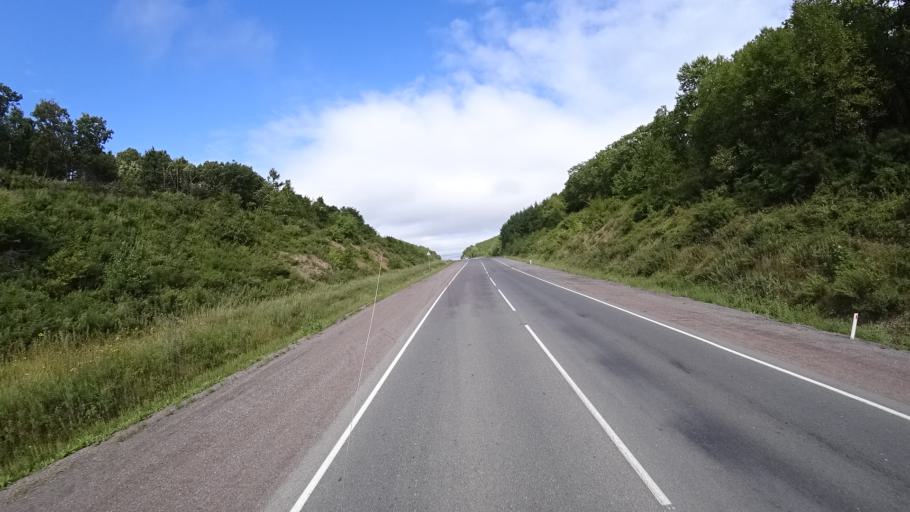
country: RU
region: Primorskiy
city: Lyalichi
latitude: 44.1227
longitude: 132.4216
